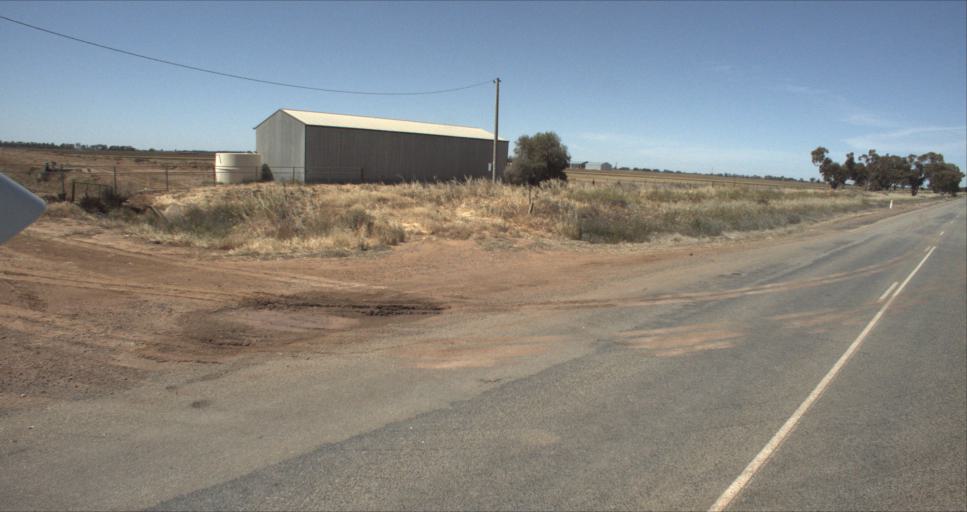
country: AU
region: New South Wales
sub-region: Leeton
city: Leeton
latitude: -34.4999
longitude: 146.2871
